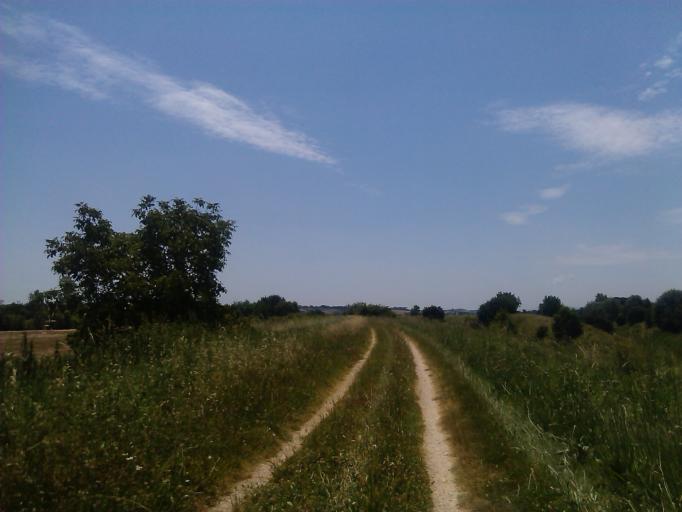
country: IT
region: Tuscany
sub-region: Province of Arezzo
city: Cesa
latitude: 43.3171
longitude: 11.8374
